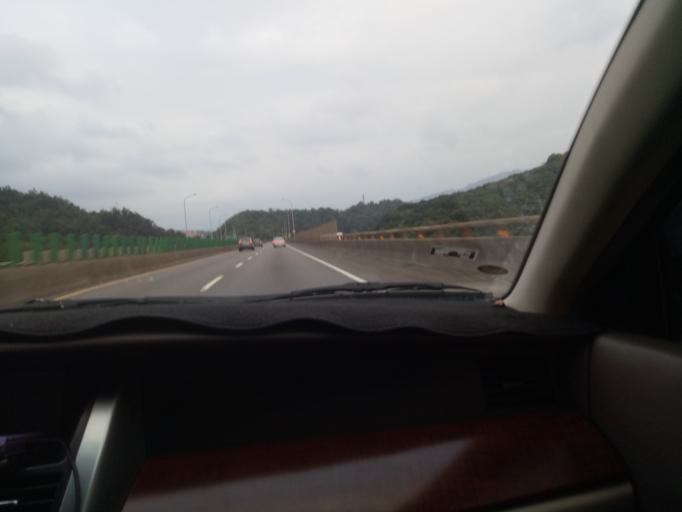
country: TW
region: Taiwan
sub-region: Keelung
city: Keelung
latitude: 25.1049
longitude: 121.7254
